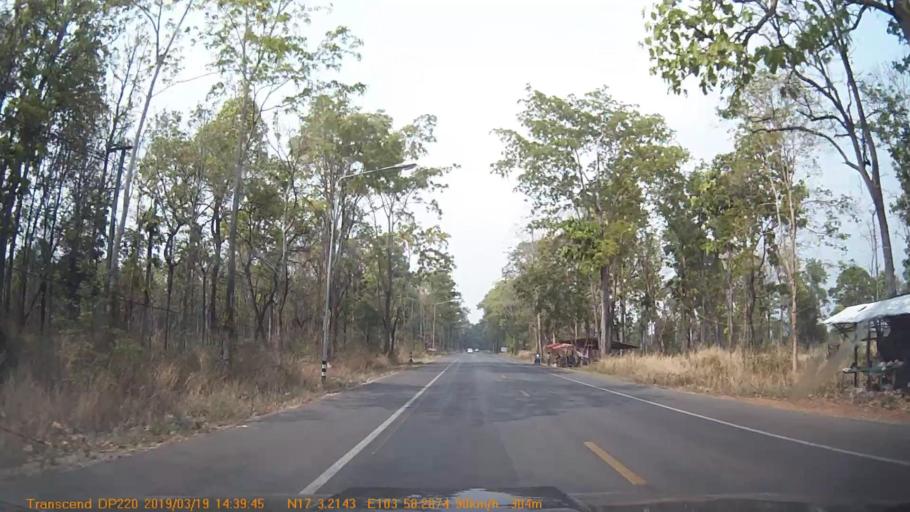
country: TH
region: Sakon Nakhon
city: Phu Phan
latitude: 17.0540
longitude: 103.9714
